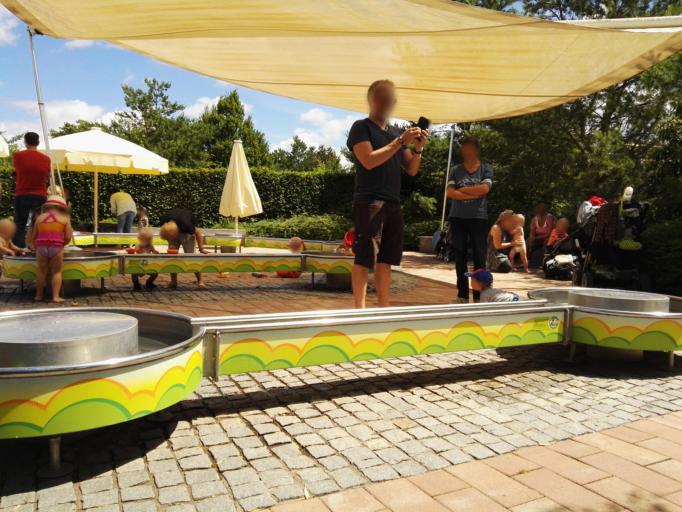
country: DE
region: Bavaria
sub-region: Regierungsbezirk Mittelfranken
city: Oberasbach
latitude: 49.4302
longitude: 10.9438
